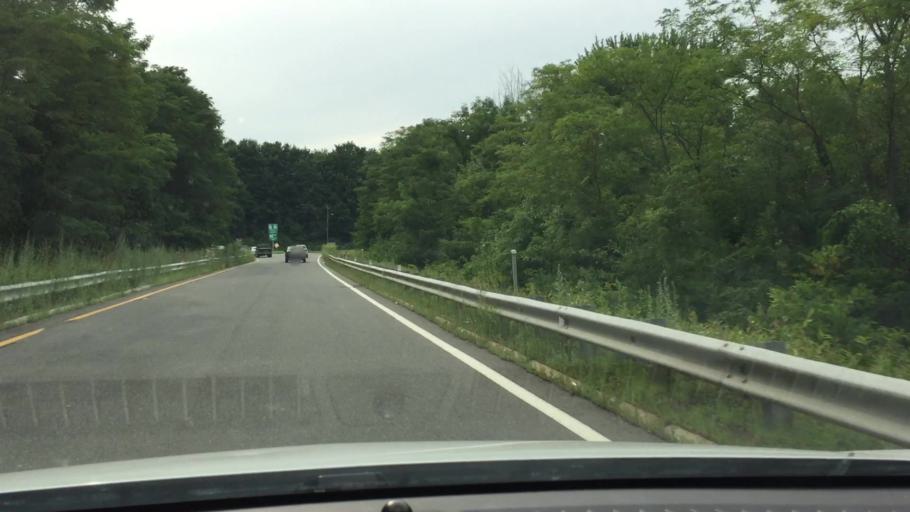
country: US
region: Massachusetts
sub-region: Hampden County
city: Agawam
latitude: 42.0570
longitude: -72.6735
